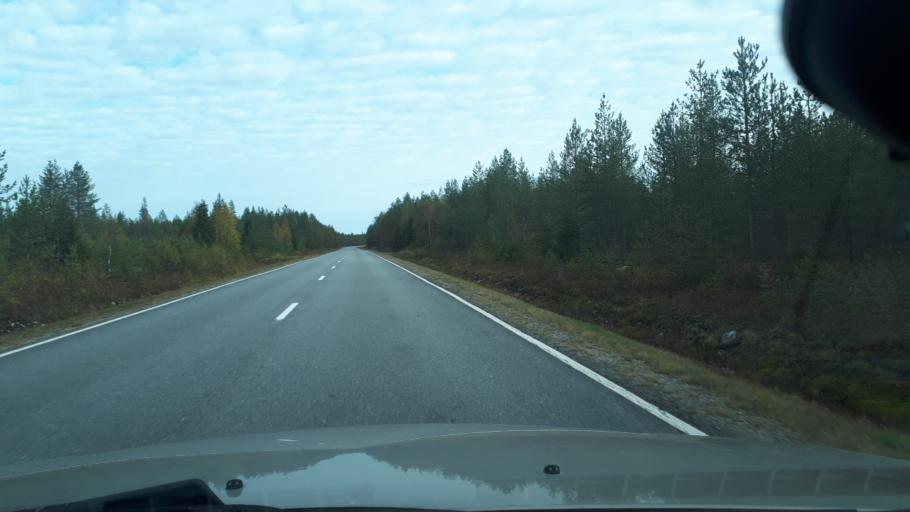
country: FI
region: Northern Ostrobothnia
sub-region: Oulu
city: Yli-Ii
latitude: 65.9055
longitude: 25.7377
